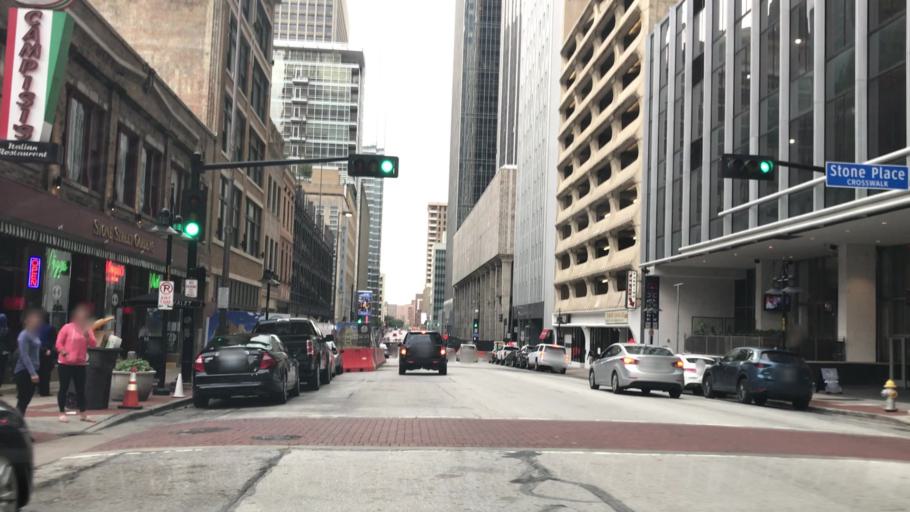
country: US
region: Texas
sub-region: Dallas County
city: Dallas
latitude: 32.7816
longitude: -96.7985
